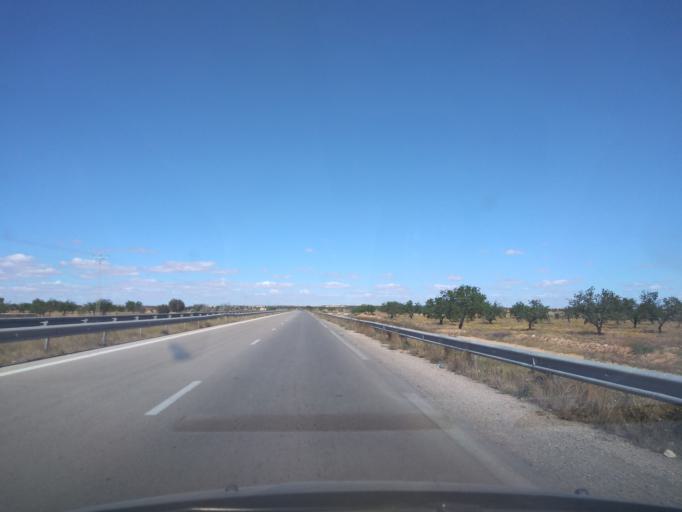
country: TN
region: Safaqis
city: Al Qarmadah
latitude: 34.8741
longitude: 10.7383
